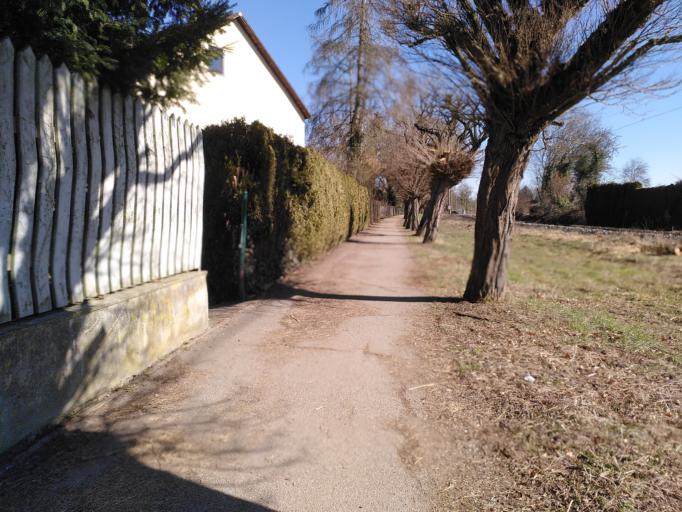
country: DE
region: Bavaria
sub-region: Upper Palatinate
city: Sinzing
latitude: 49.0116
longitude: 12.0413
